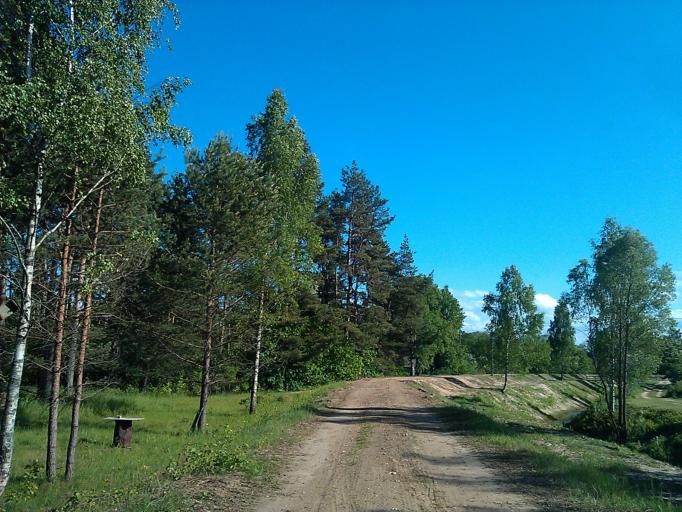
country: LV
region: Adazi
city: Adazi
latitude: 57.0979
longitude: 24.3294
